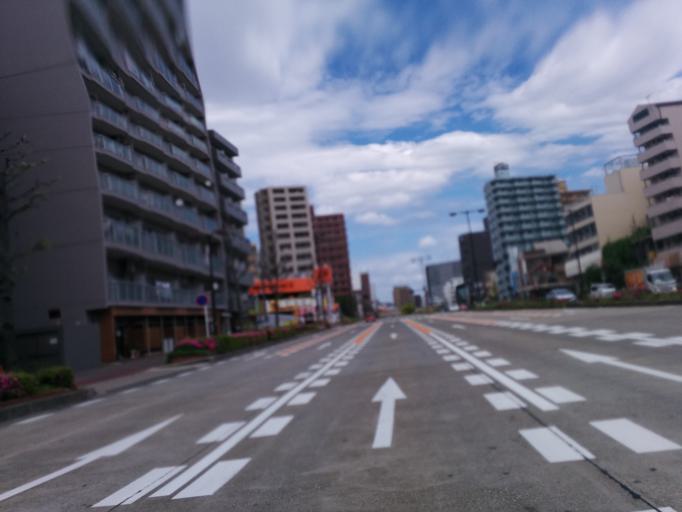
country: JP
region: Aichi
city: Nagoya-shi
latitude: 35.1854
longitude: 136.9253
